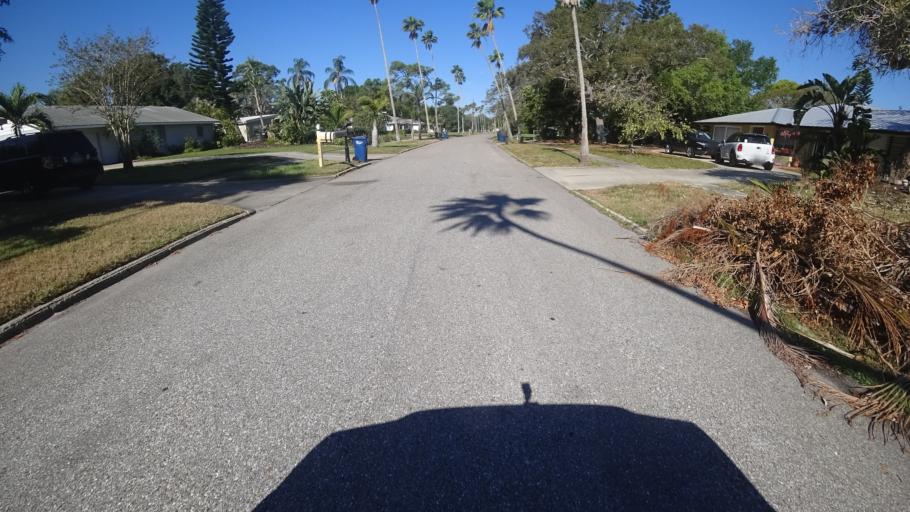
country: US
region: Florida
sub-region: Manatee County
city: West Bradenton
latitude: 27.4949
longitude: -82.6392
